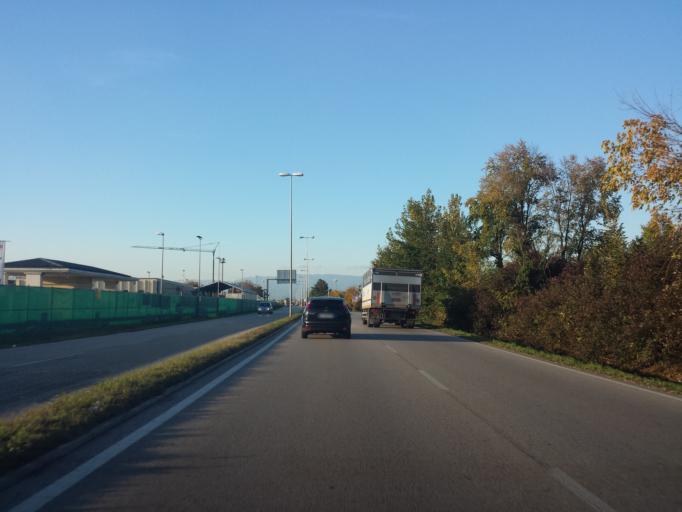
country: IT
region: Veneto
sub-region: Provincia di Vicenza
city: Villaggio Montegrappa
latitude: 45.5452
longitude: 11.5856
